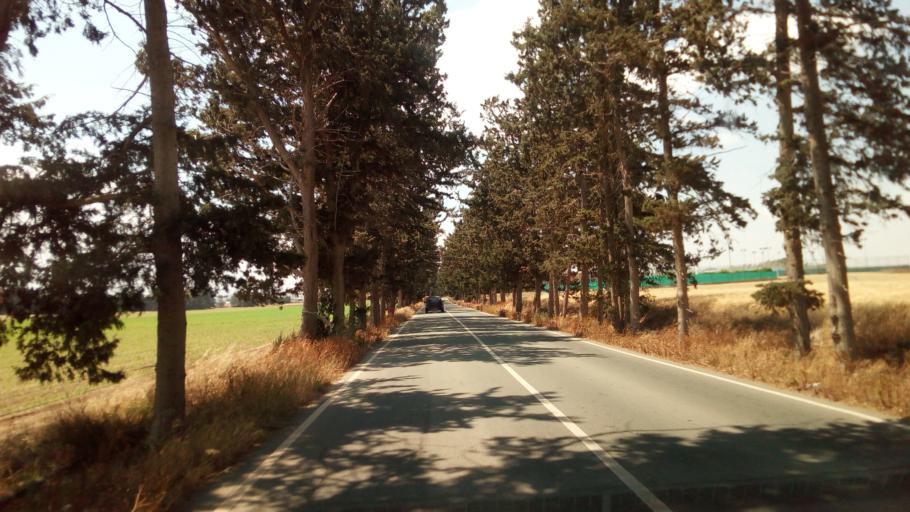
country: CY
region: Larnaka
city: Meneou
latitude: 34.8536
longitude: 33.6054
